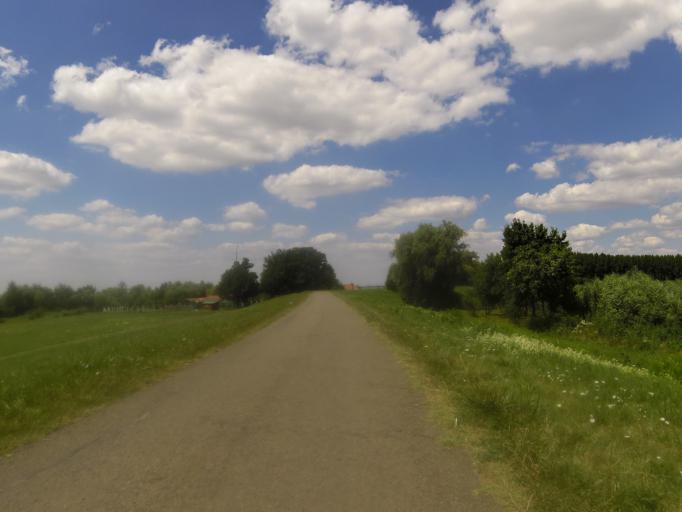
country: HU
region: Heves
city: Tiszanana
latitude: 47.5682
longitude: 20.6085
